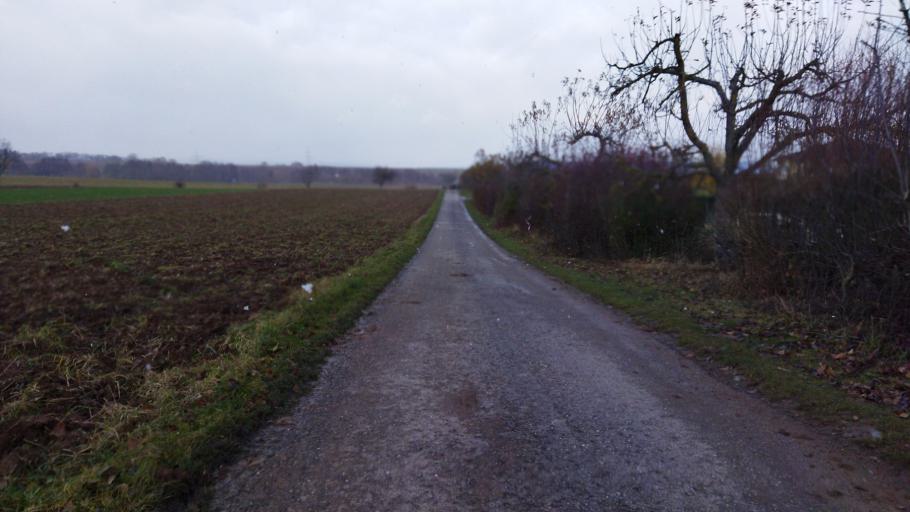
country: DE
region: Baden-Wuerttemberg
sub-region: Regierungsbezirk Stuttgart
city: Erligheim
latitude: 49.0203
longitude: 9.0880
